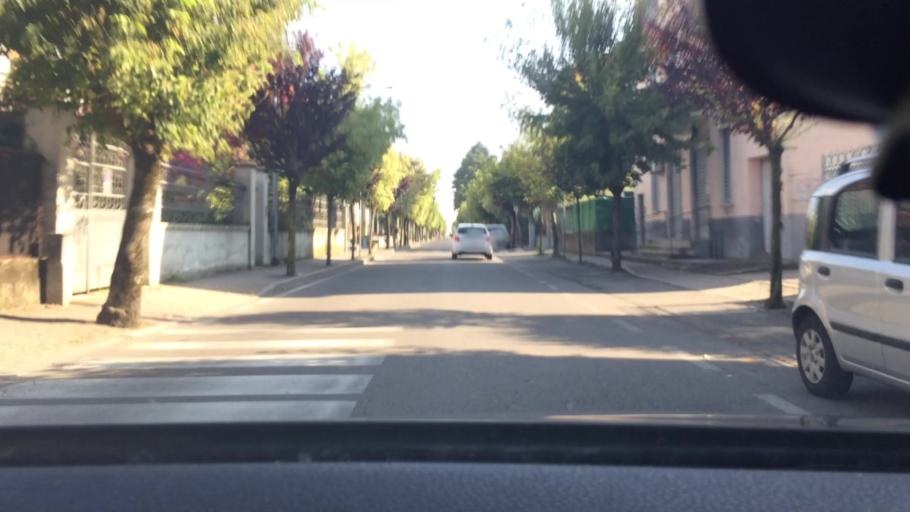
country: IT
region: Lombardy
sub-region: Provincia di Como
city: Turate
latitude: 45.6507
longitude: 9.0014
